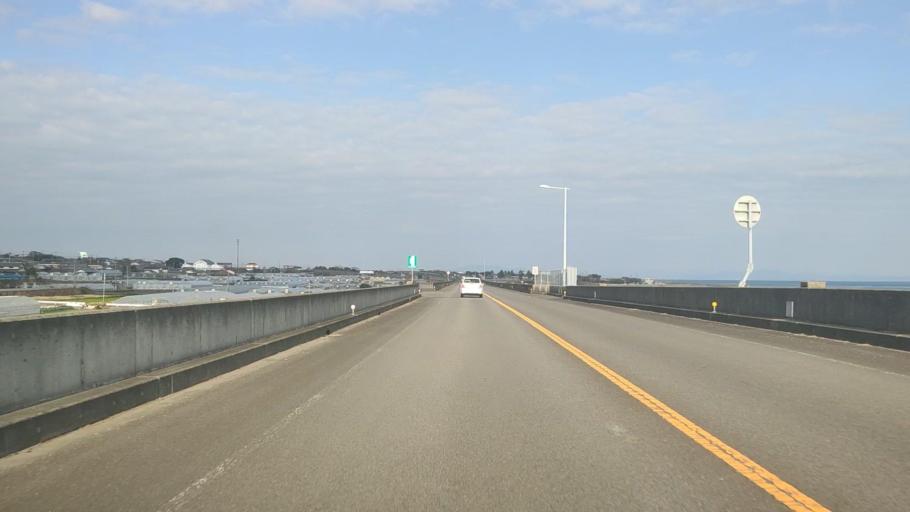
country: JP
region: Nagasaki
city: Shimabara
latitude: 32.7297
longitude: 130.3660
